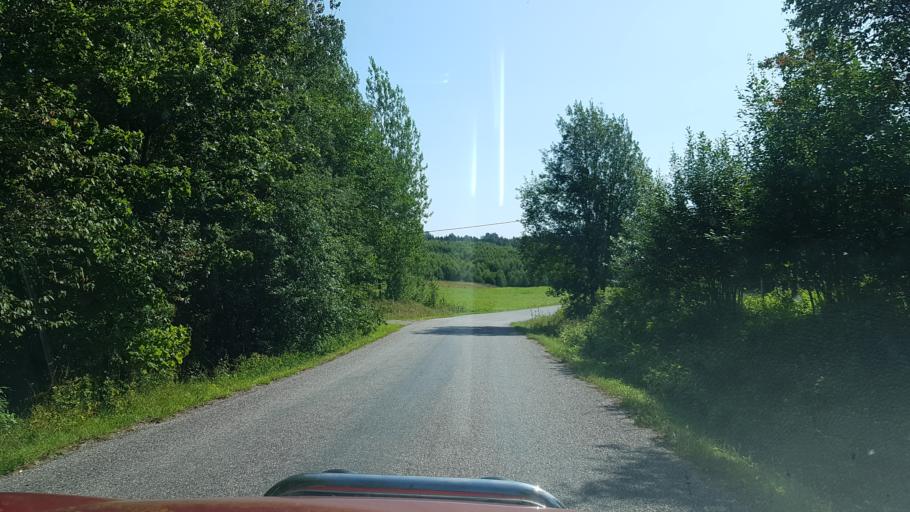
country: EE
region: Vorumaa
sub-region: Voru linn
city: Voru
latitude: 57.7201
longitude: 27.1056
